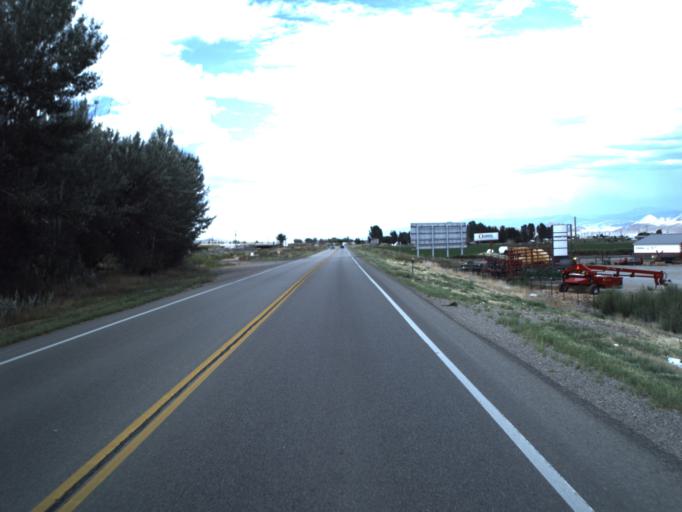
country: US
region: Utah
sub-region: Sevier County
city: Richfield
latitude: 38.7751
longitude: -112.0662
